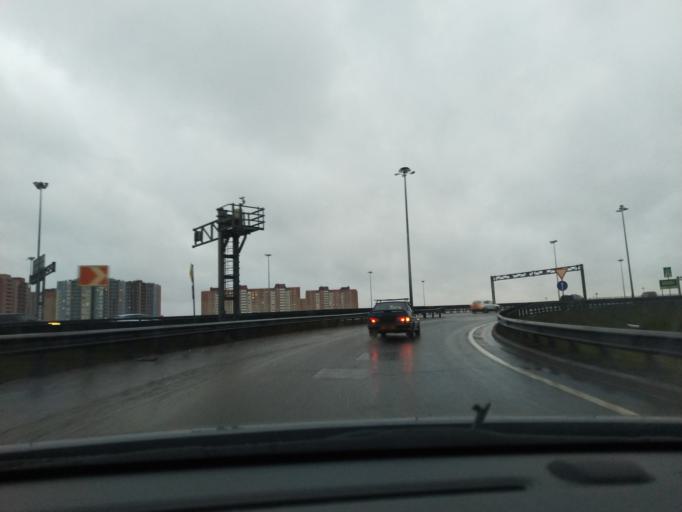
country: RU
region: St.-Petersburg
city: Sosnovaya Polyana
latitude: 59.8000
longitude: 30.1603
